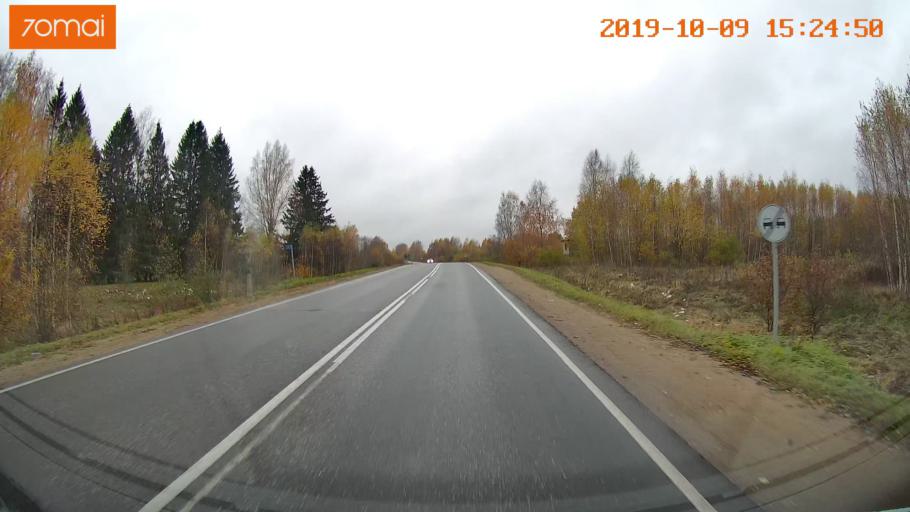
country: RU
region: Kostroma
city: Susanino
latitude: 58.0303
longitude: 41.4435
